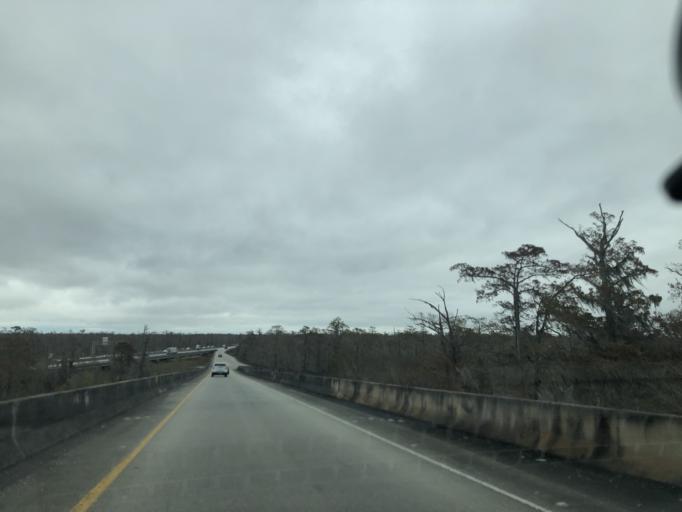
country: US
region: Louisiana
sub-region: Saint Charles Parish
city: Saint Rose
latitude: 29.9765
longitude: -90.3157
